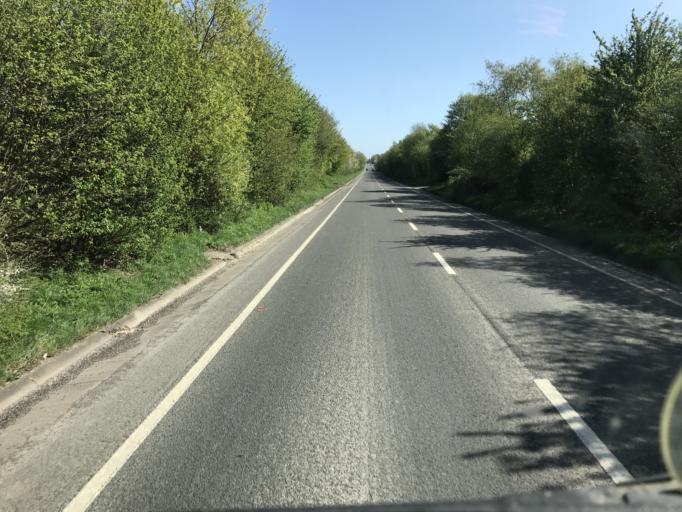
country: GB
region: England
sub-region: Cheshire East
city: Nantwich
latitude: 53.0767
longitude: -2.5048
